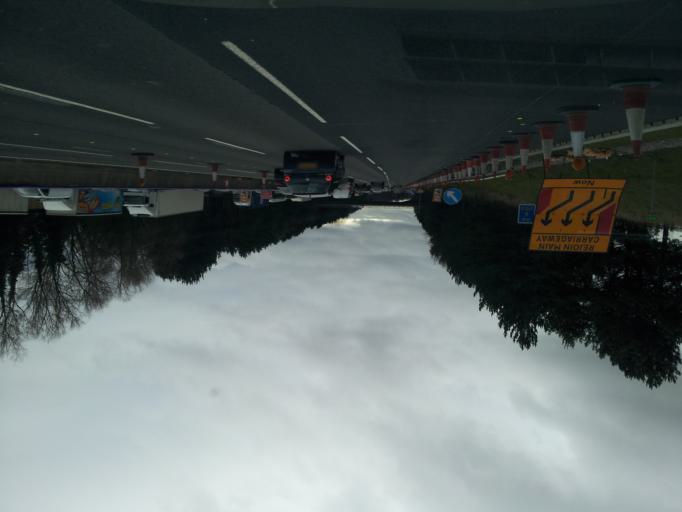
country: GB
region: England
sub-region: Staffordshire
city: Penkridge
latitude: 52.7254
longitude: -2.1000
